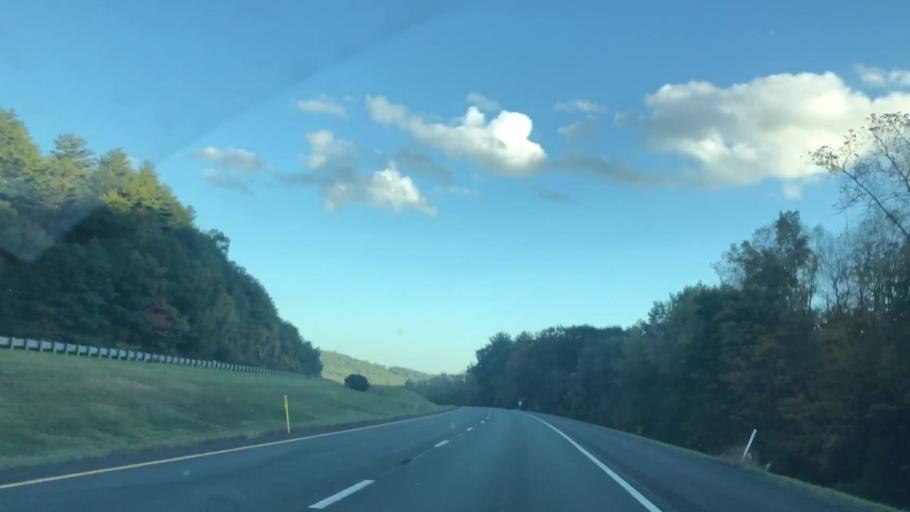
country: US
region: Massachusetts
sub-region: Franklin County
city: Bernardston
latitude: 42.7029
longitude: -72.5583
